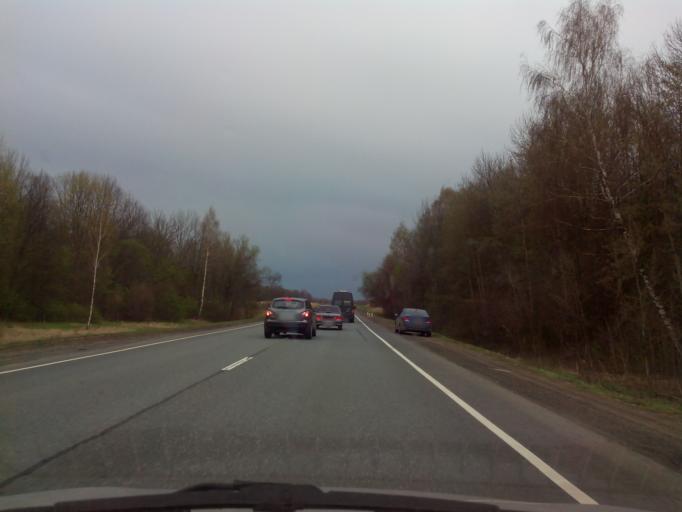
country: RU
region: Moskovskaya
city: Uzunovo
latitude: 54.5562
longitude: 38.4614
